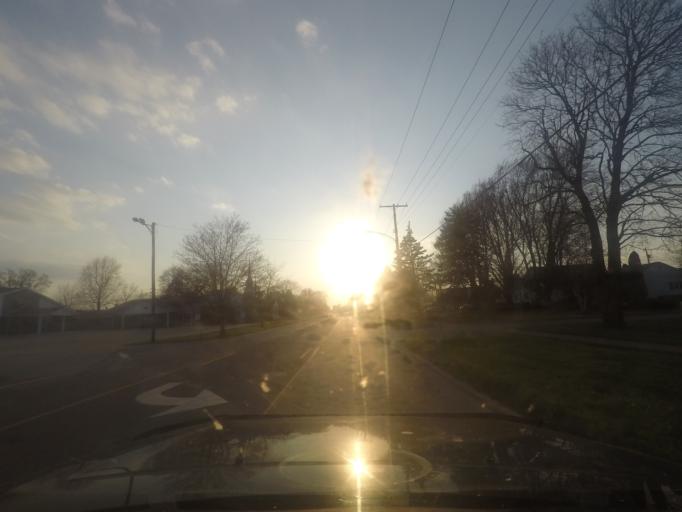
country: US
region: Indiana
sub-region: LaPorte County
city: LaPorte
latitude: 41.5915
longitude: -86.7182
